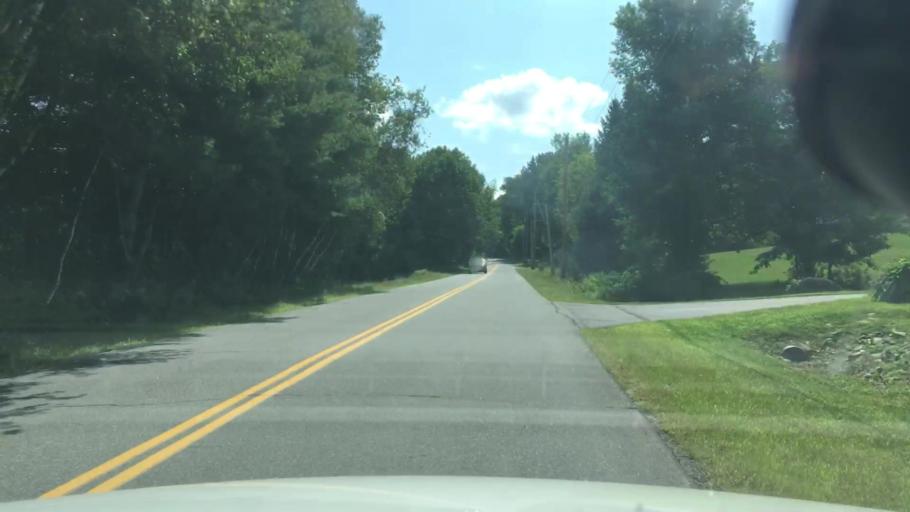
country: US
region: Maine
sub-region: Somerset County
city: Skowhegan
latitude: 44.7357
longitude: -69.7108
